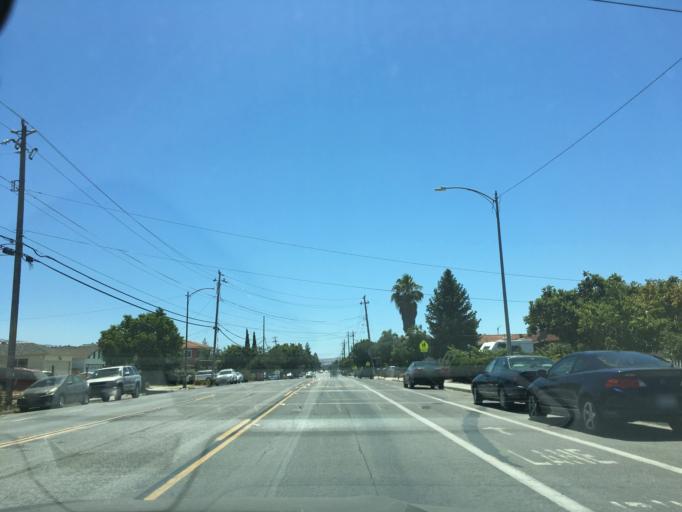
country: US
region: California
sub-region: Santa Clara County
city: Alum Rock
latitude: 37.3807
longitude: -121.8399
